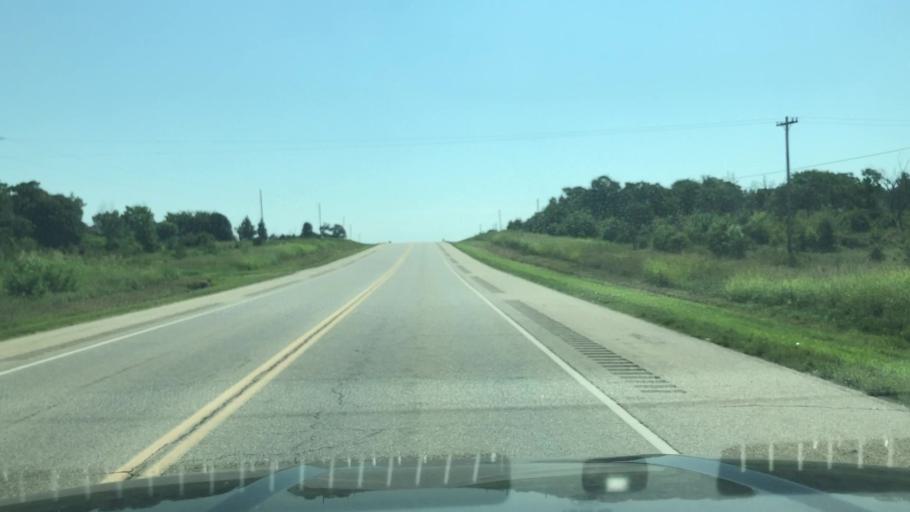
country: US
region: Oklahoma
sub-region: Creek County
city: Mannford
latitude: 36.0031
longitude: -96.4367
